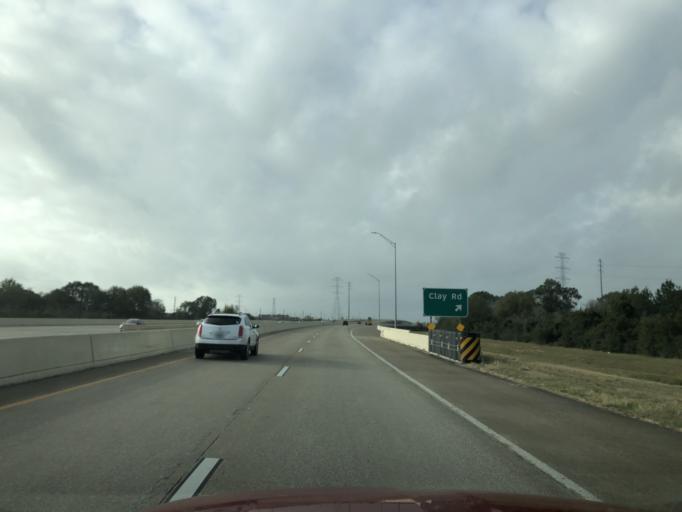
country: US
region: Texas
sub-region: Harris County
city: Katy
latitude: 29.8375
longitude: -95.7575
